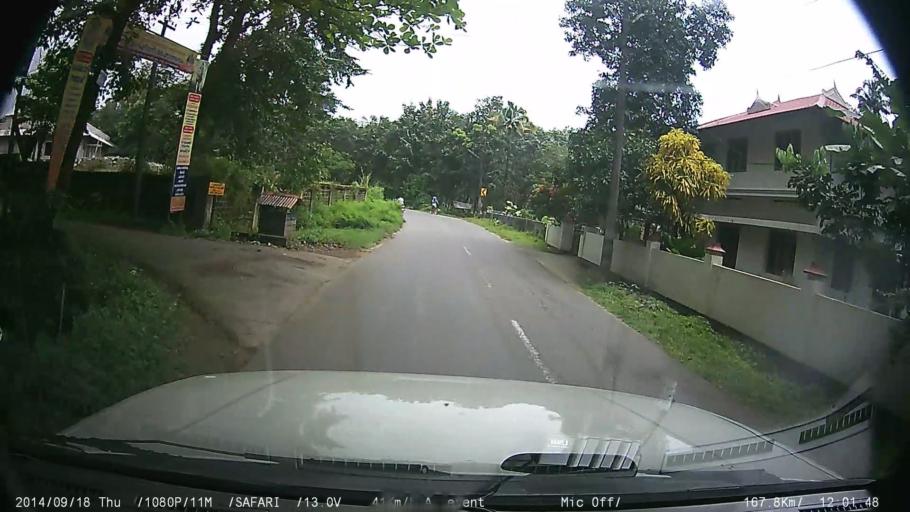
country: IN
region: Kerala
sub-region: Ernakulam
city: Kotamangalam
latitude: 10.1060
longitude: 76.6694
